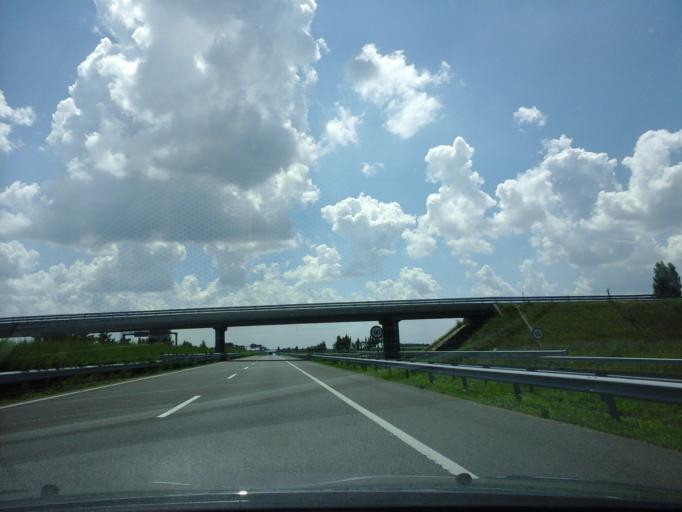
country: HU
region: Hajdu-Bihar
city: Debrecen
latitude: 47.5350
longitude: 21.5518
